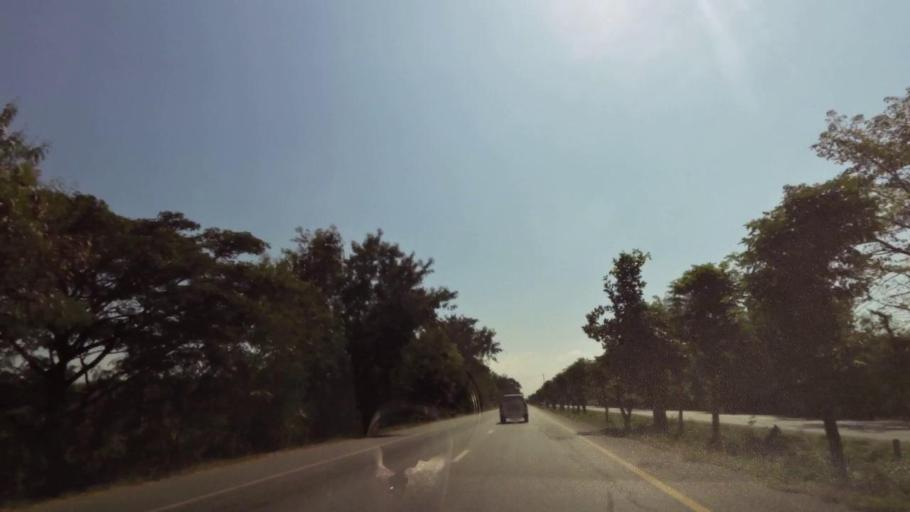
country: TH
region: Nakhon Sawan
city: Kao Liao
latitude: 15.7902
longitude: 100.1209
